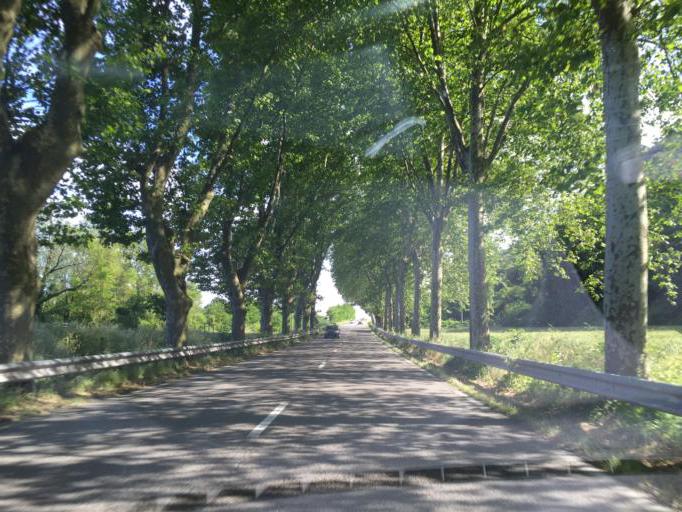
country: FR
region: Rhone-Alpes
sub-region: Departement de l'Ardeche
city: Cruas
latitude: 44.6840
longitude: 4.7719
